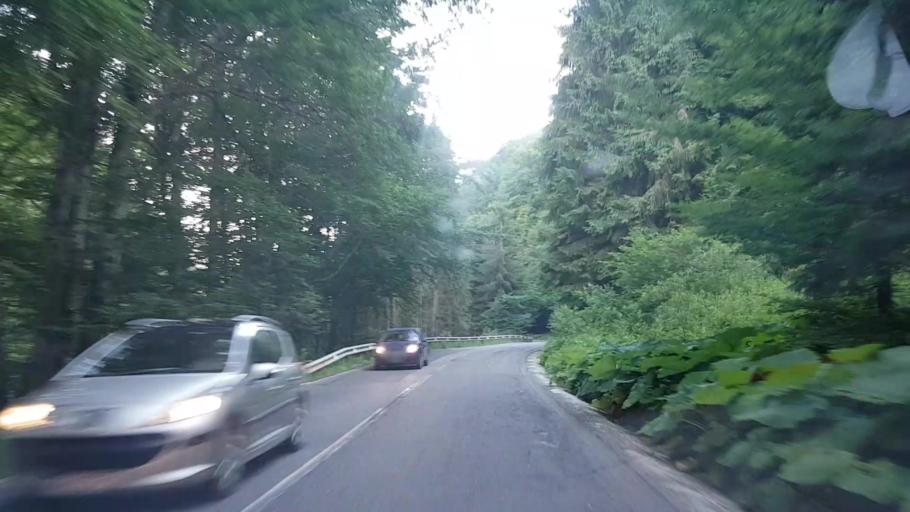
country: RO
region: Harghita
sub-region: Comuna Praid
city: Ocna de Sus
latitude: 46.6010
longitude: 25.2391
